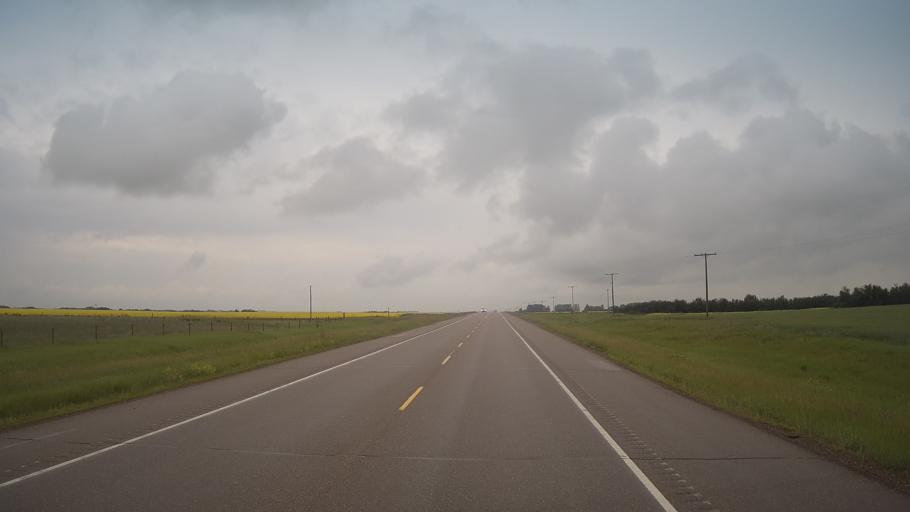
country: CA
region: Saskatchewan
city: Unity
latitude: 52.4349
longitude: -108.9507
